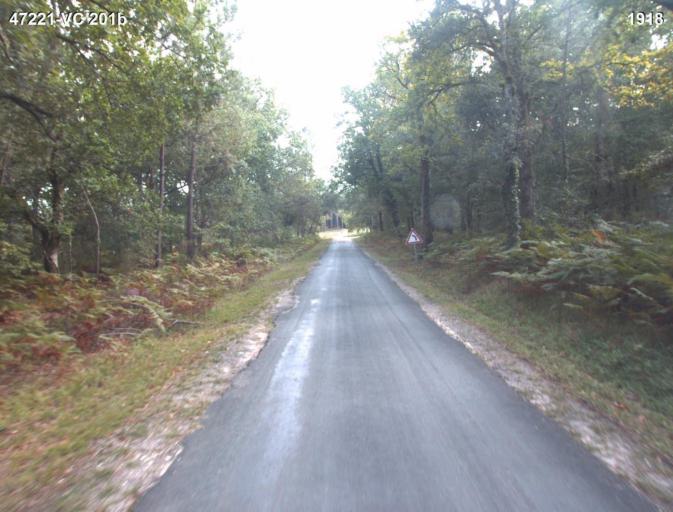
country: FR
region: Aquitaine
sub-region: Departement du Lot-et-Garonne
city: Mezin
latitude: 44.0814
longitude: 0.2280
